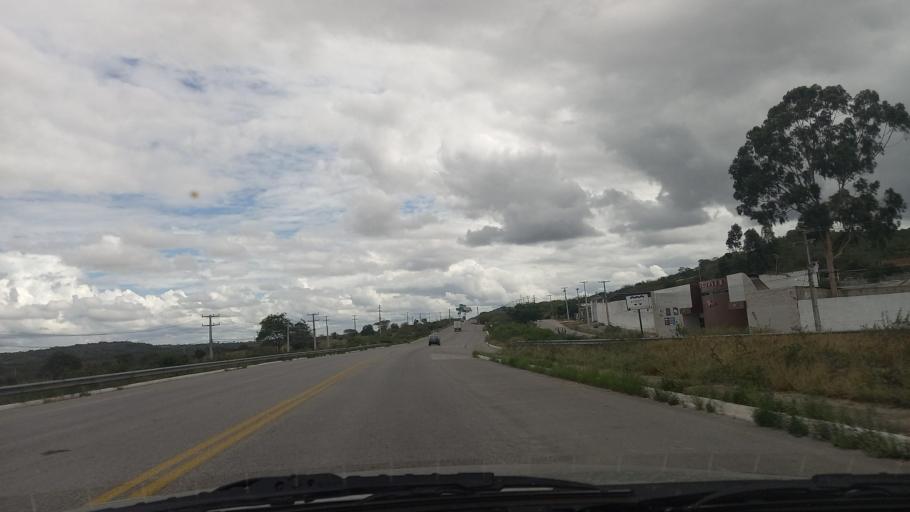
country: BR
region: Pernambuco
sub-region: Caruaru
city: Caruaru
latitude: -8.3305
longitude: -36.1475
